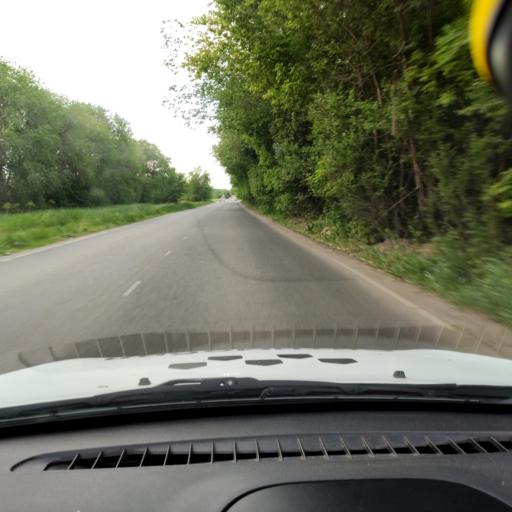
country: RU
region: Samara
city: Tol'yatti
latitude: 53.5756
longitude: 49.2549
